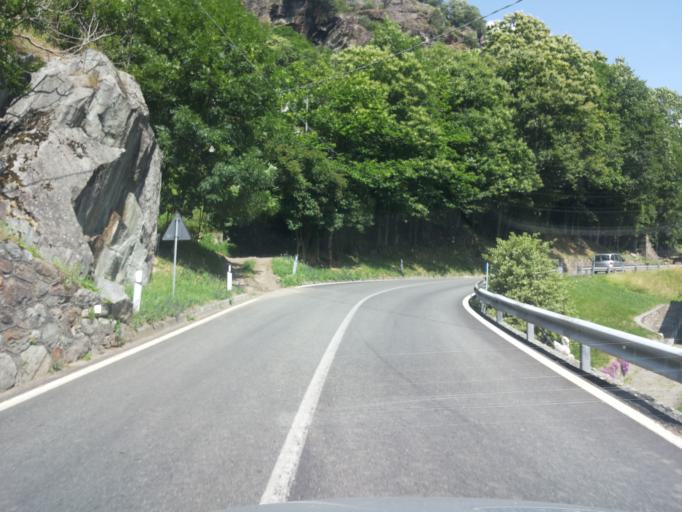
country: IT
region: Aosta Valley
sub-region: Valle d'Aosta
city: Fontainemore
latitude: 45.6630
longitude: 7.8579
